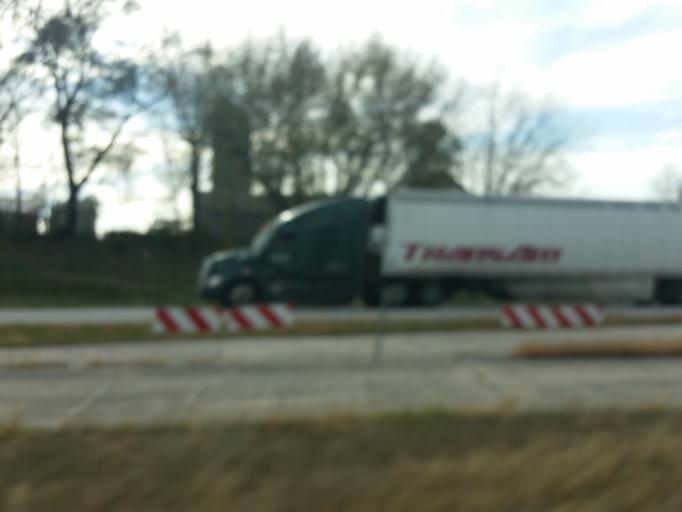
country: US
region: Illinois
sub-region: Henry County
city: Green Rock
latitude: 41.4408
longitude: -90.3494
